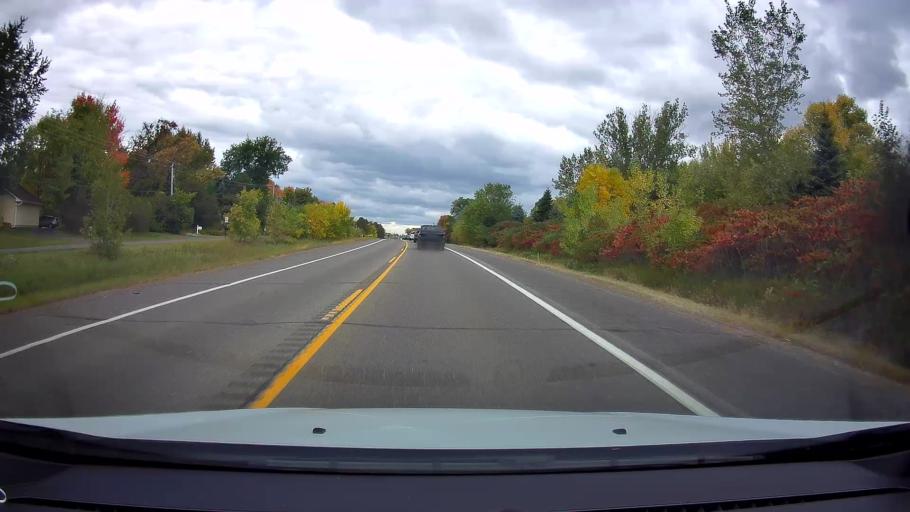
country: US
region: Minnesota
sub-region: Chisago County
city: Chisago City
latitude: 45.3621
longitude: -92.9068
